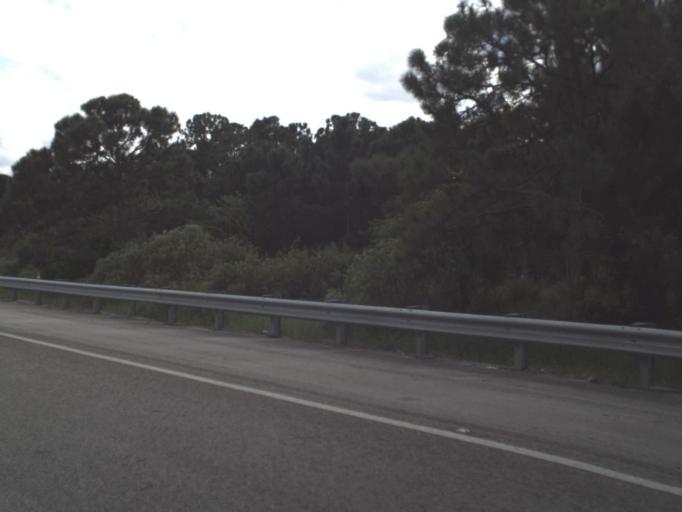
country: US
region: Florida
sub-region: Saint Lucie County
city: Port Saint Lucie
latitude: 27.2748
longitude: -80.3593
